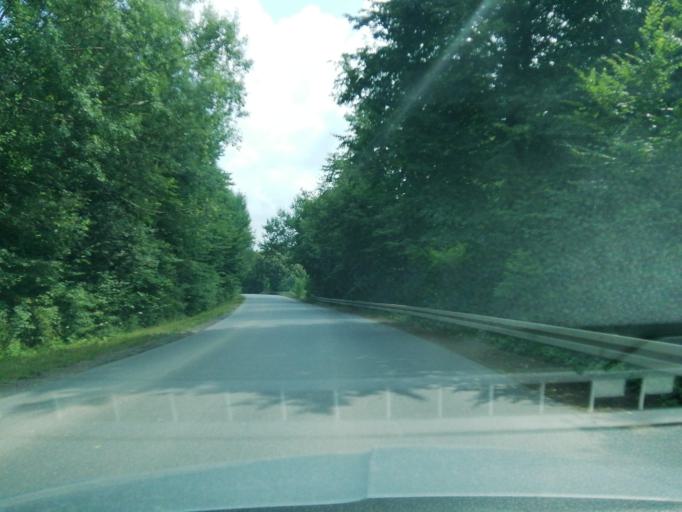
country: PL
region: Silesian Voivodeship
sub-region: Powiat zywiecki
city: Radziechowy
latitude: 49.6263
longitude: 19.1414
